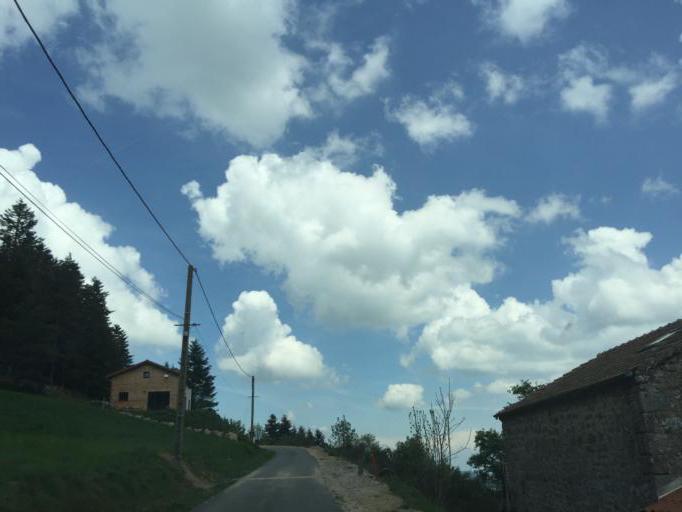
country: FR
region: Rhone-Alpes
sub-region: Departement de la Loire
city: Saint-Sauveur-en-Rue
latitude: 45.2761
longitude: 4.4729
